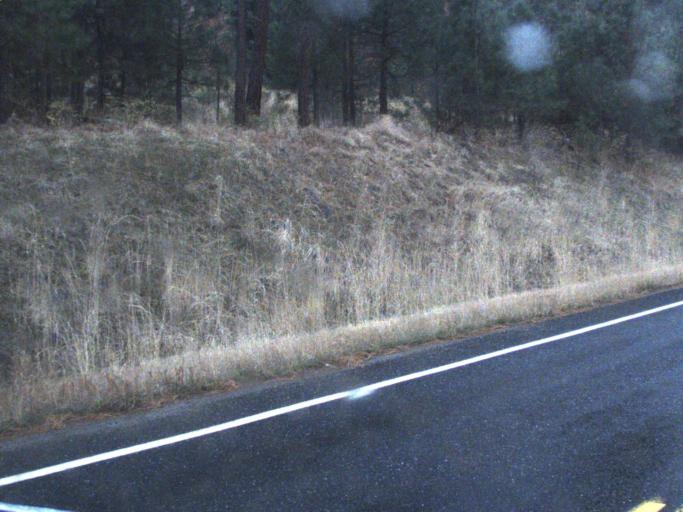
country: US
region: Washington
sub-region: Stevens County
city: Kettle Falls
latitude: 48.4958
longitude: -118.1611
